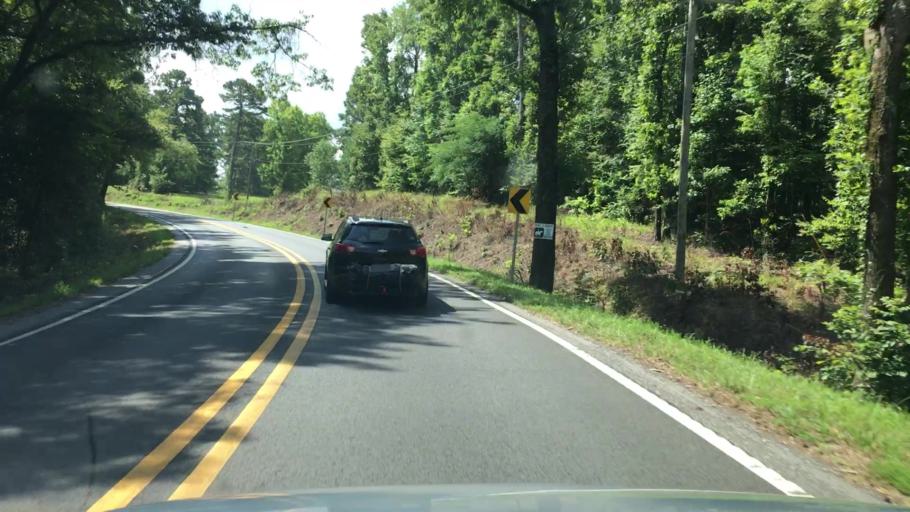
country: US
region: Arkansas
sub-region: Clark County
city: Arkadelphia
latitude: 34.2575
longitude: -93.1303
